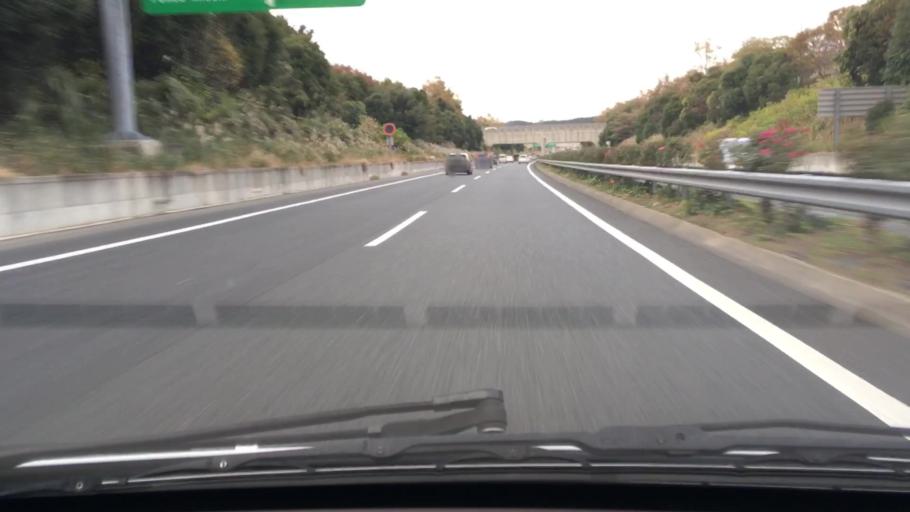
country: JP
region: Chiba
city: Kisarazu
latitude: 35.3386
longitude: 139.9444
